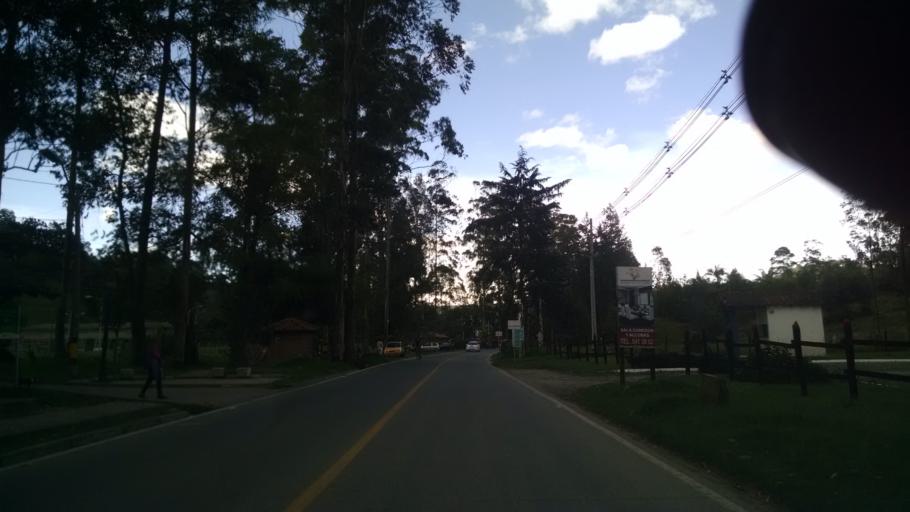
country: CO
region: Antioquia
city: El Retiro
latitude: 6.0692
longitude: -75.4999
